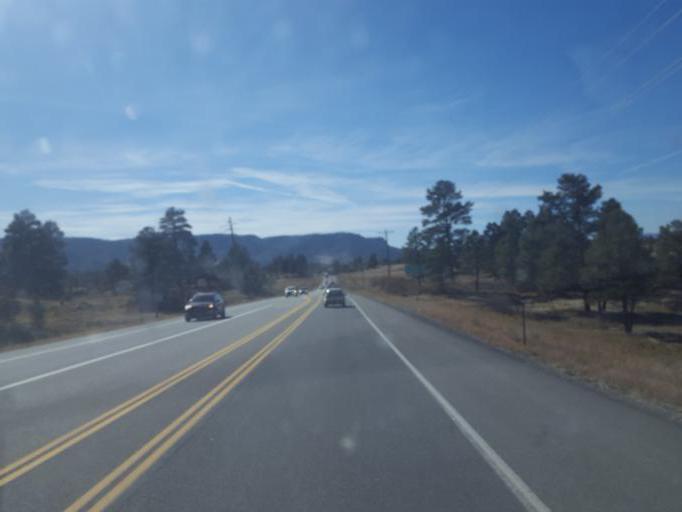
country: US
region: Colorado
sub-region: Archuleta County
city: Pagosa Springs
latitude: 37.2480
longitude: -107.0891
